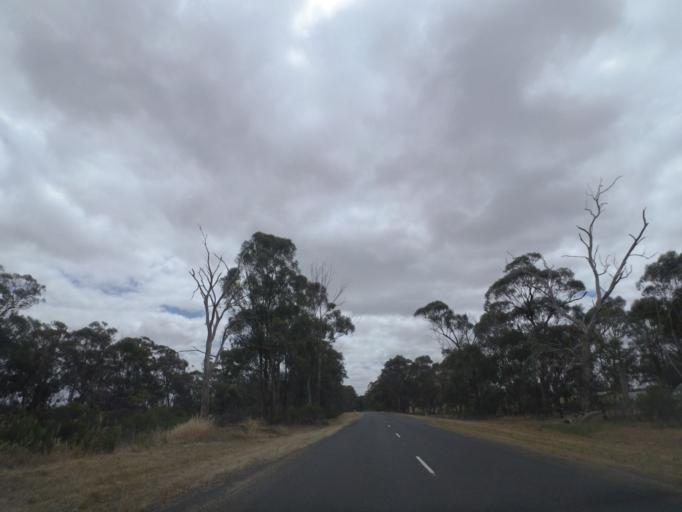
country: AU
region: Victoria
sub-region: Murrindindi
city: Kinglake West
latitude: -36.9824
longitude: 145.1607
